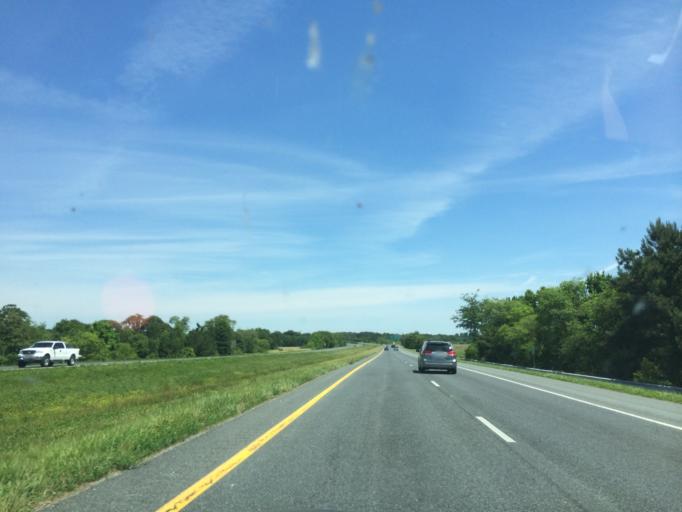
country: US
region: Maryland
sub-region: Wicomico County
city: Salisbury
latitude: 38.3582
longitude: -75.5395
